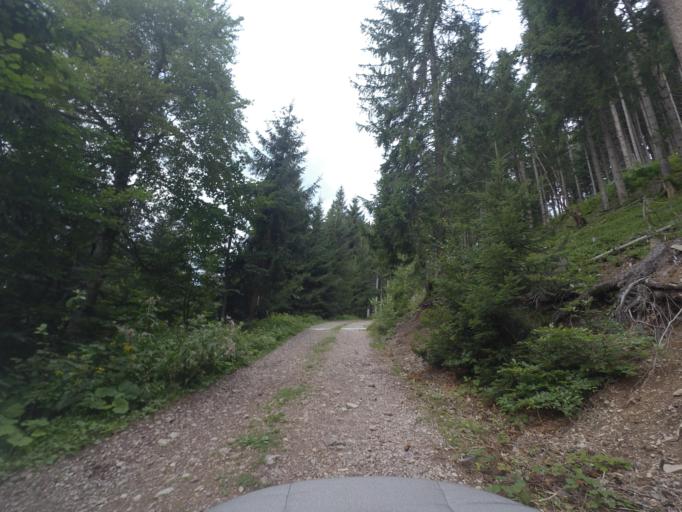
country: AT
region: Salzburg
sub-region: Politischer Bezirk Sankt Johann im Pongau
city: Werfenweng
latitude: 47.4717
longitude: 13.2370
